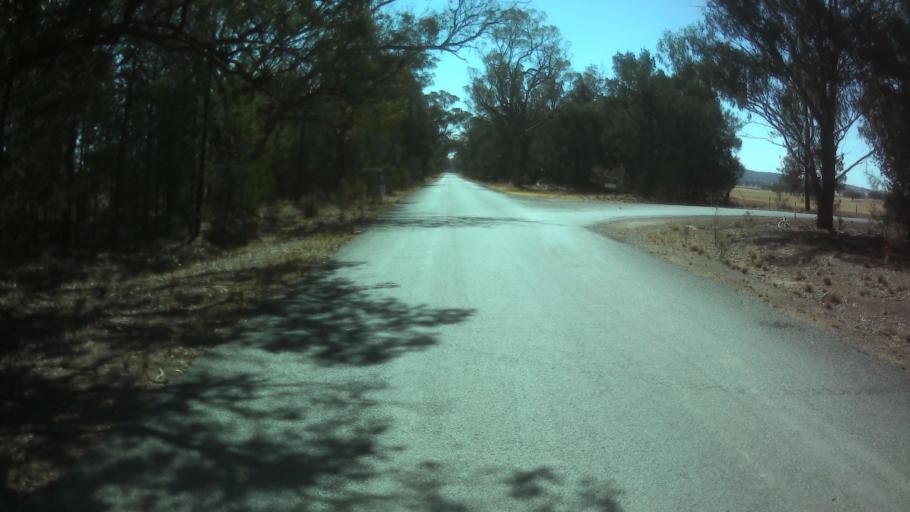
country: AU
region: New South Wales
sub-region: Weddin
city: Grenfell
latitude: -33.8141
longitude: 147.9284
